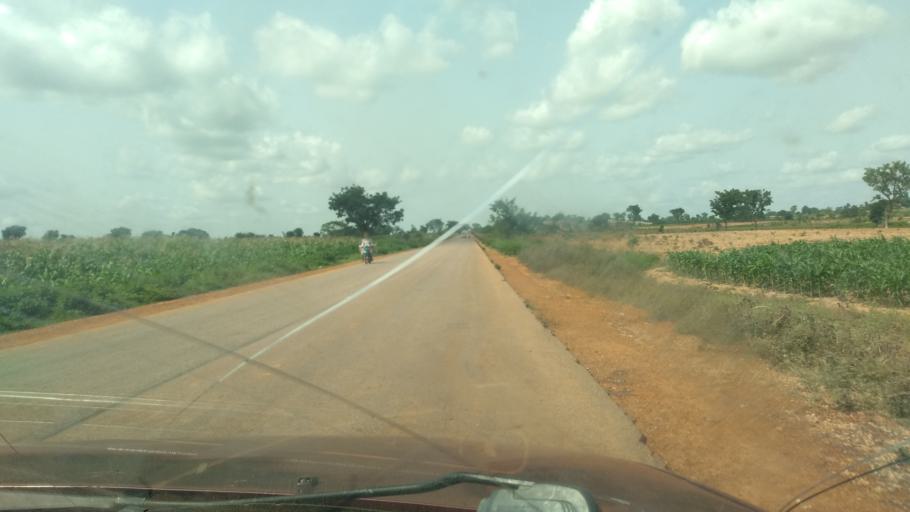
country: NG
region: Katsina
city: Sabuwa
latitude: 11.0497
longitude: 7.1580
